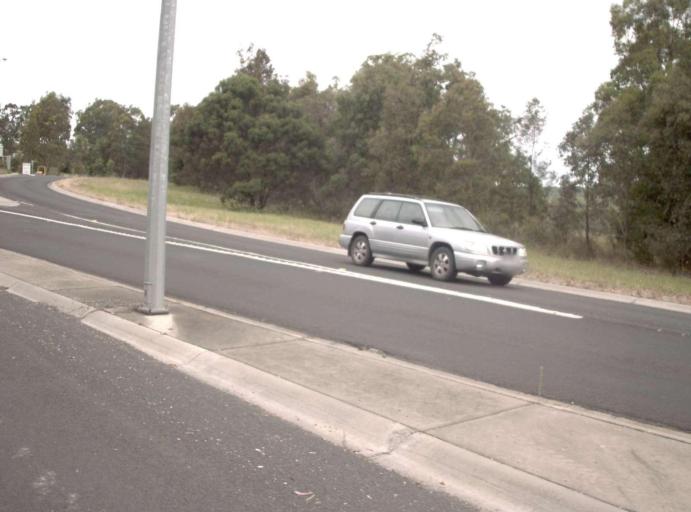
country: AU
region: Victoria
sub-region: East Gippsland
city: Lakes Entrance
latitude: -37.7211
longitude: 147.8466
